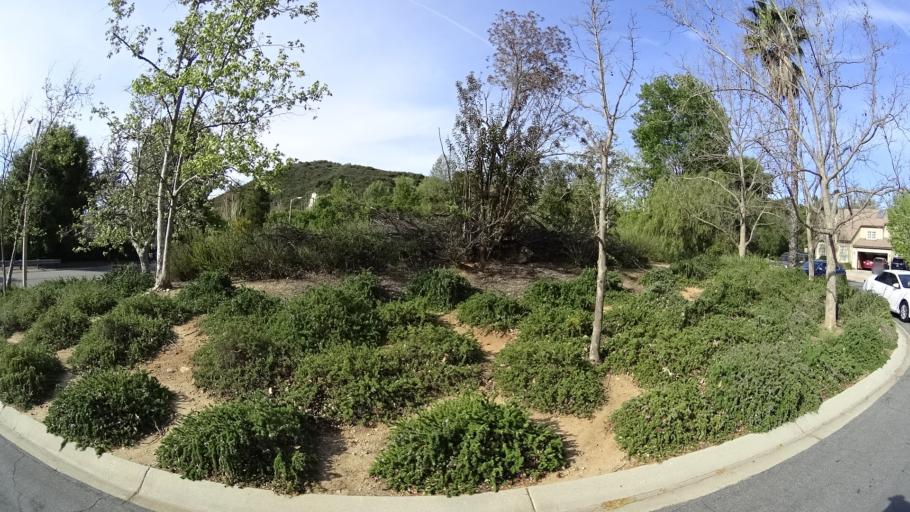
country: US
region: California
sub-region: Ventura County
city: Oak Park
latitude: 34.1948
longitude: -118.7883
